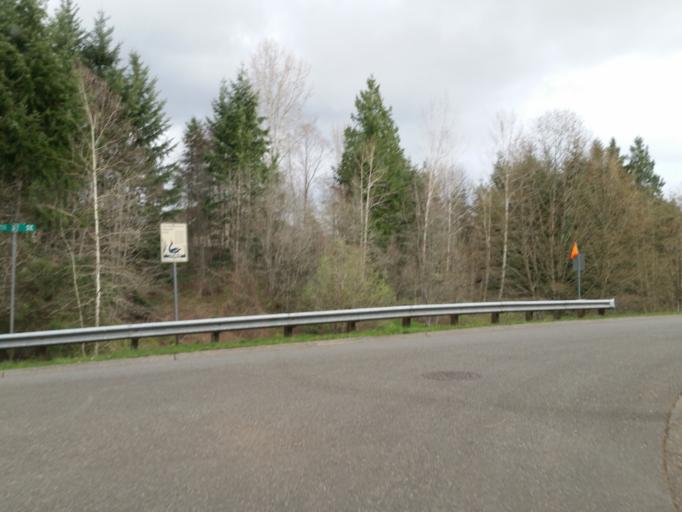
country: US
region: Washington
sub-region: Snohomish County
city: North Creek
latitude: 47.8064
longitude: -122.1915
